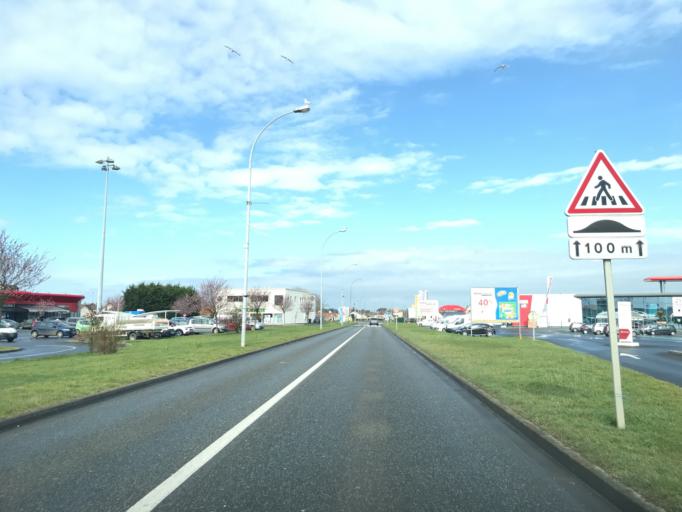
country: FR
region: Lower Normandy
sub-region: Departement du Calvados
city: Dives-sur-Mer
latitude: 49.2780
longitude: -0.1026
